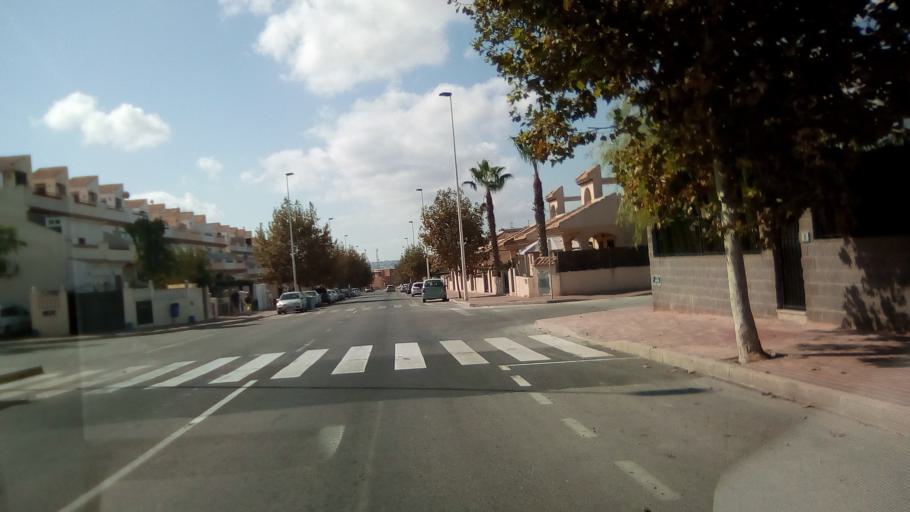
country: ES
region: Valencia
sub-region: Provincia de Alicante
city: Torrevieja
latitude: 38.0012
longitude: -0.6756
